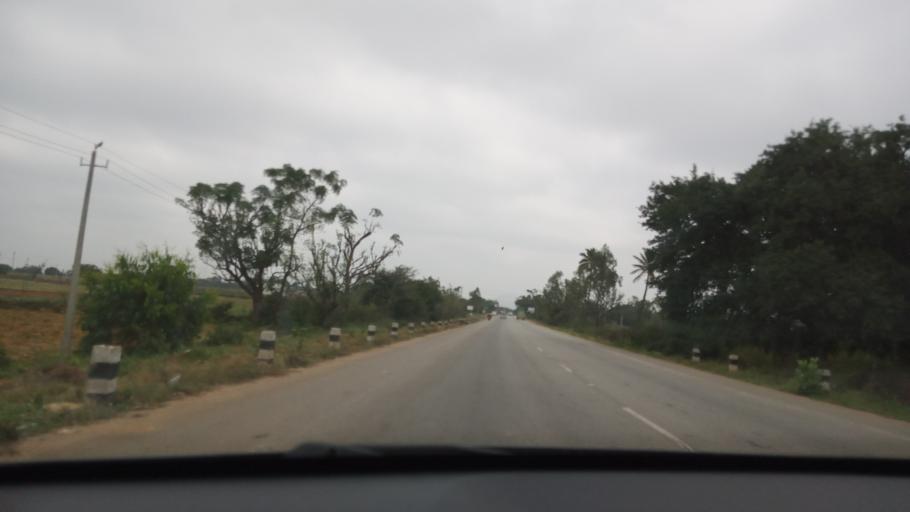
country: IN
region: Karnataka
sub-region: Chikkaballapur
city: Sidlaghatta
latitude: 13.2796
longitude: 77.9557
